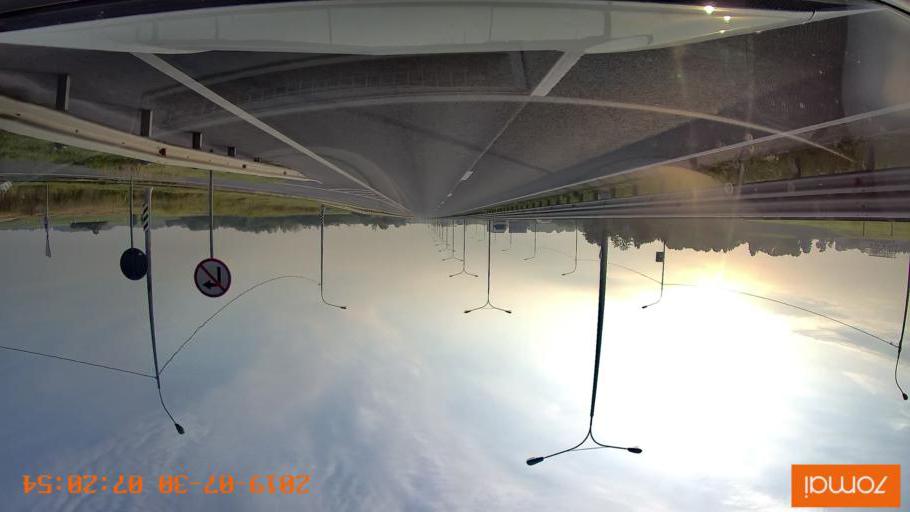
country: RU
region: Kaliningrad
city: Bol'shoe Isakovo
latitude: 54.6988
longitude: 20.7138
